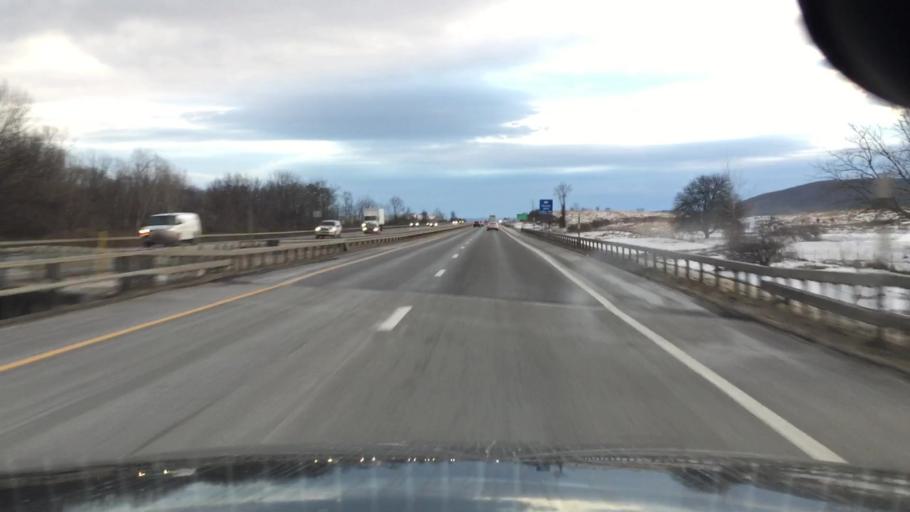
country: US
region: New York
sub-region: Chemung County
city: Big Flats
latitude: 42.1461
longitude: -76.9238
